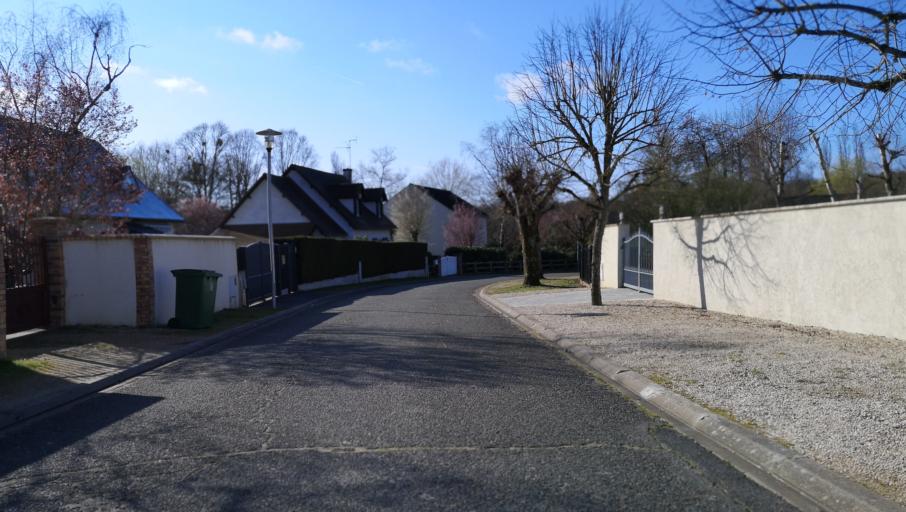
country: FR
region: Centre
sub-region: Departement du Loiret
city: Chanteau
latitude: 47.9620
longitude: 1.9684
